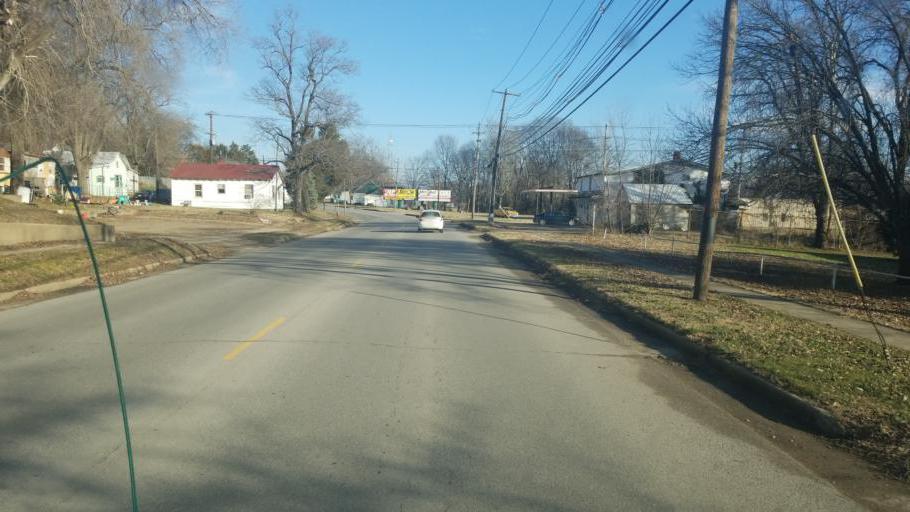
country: US
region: Illinois
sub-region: Wabash County
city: Mount Carmel
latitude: 38.4034
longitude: -87.7752
